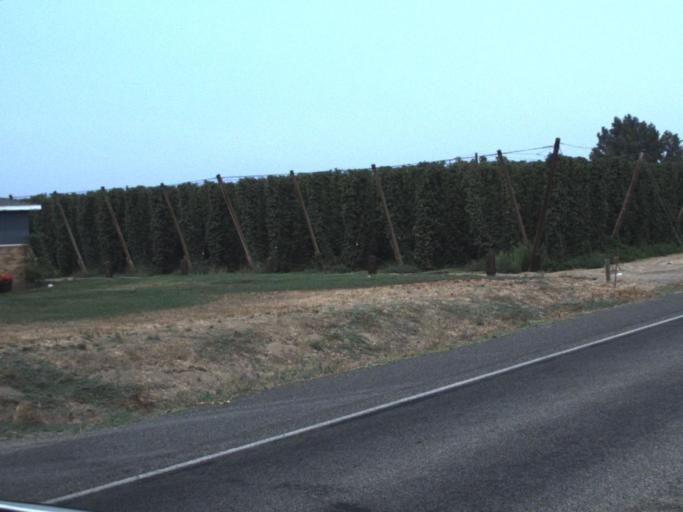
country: US
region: Washington
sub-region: Yakima County
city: Mabton
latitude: 46.2533
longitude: -119.9994
